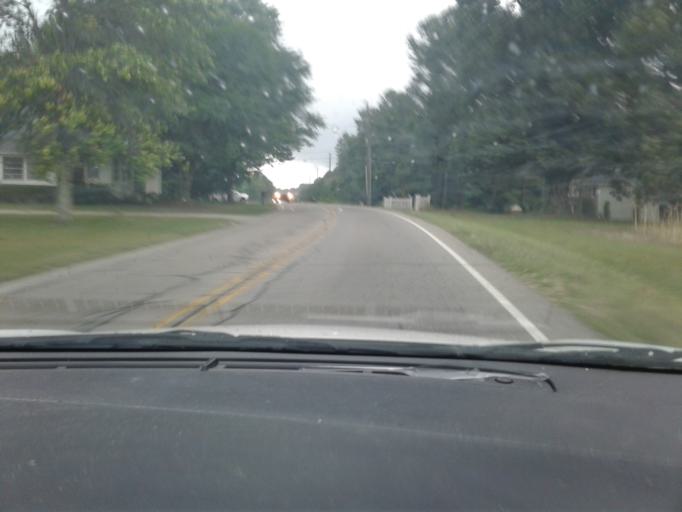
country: US
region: North Carolina
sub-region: Wake County
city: Fuquay-Varina
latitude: 35.5894
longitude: -78.8385
